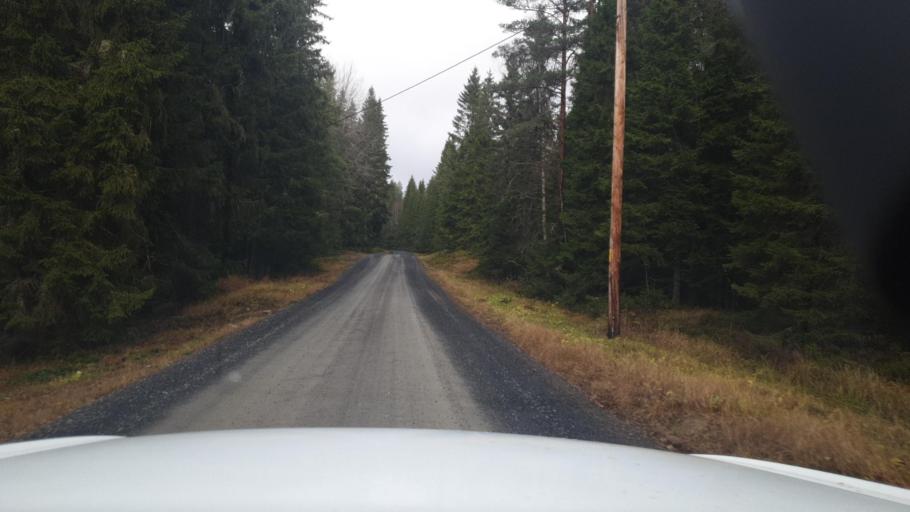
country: SE
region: Vaermland
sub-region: Eda Kommun
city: Charlottenberg
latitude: 60.1415
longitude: 12.5960
